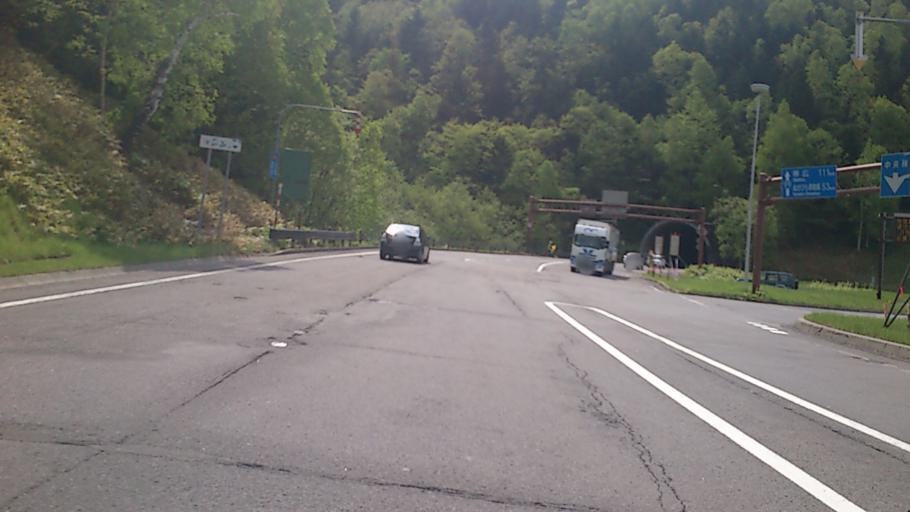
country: JP
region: Hokkaido
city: Kamikawa
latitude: 43.6811
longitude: 143.0365
